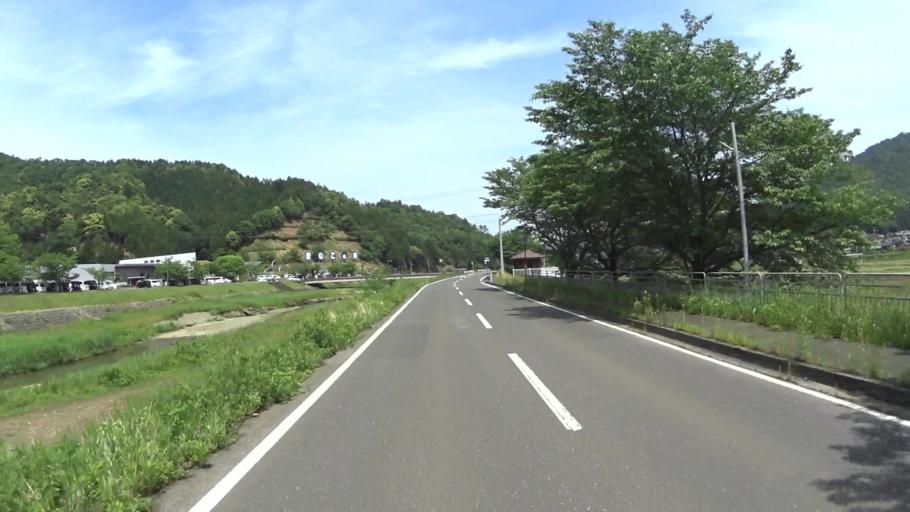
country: JP
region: Fukui
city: Obama
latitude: 35.4522
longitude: 135.5640
